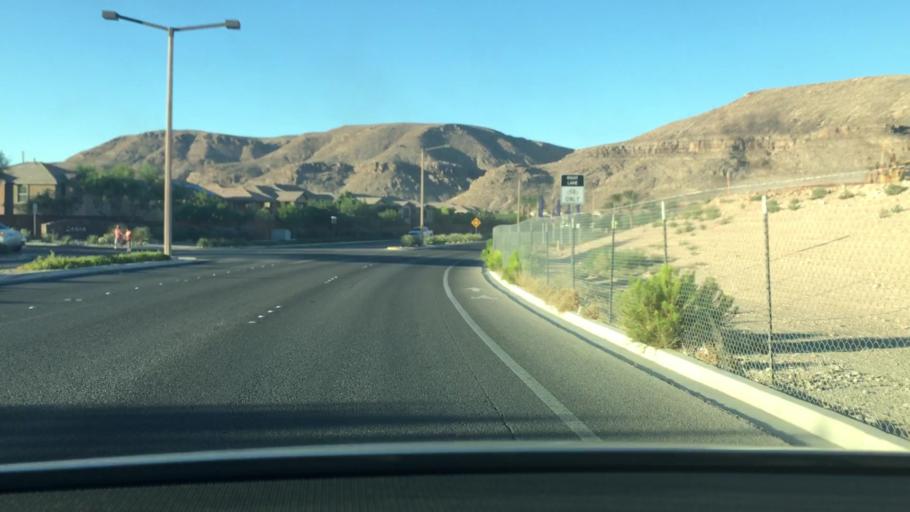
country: US
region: Nevada
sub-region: Clark County
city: Summerlin South
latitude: 36.0925
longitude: -115.3245
